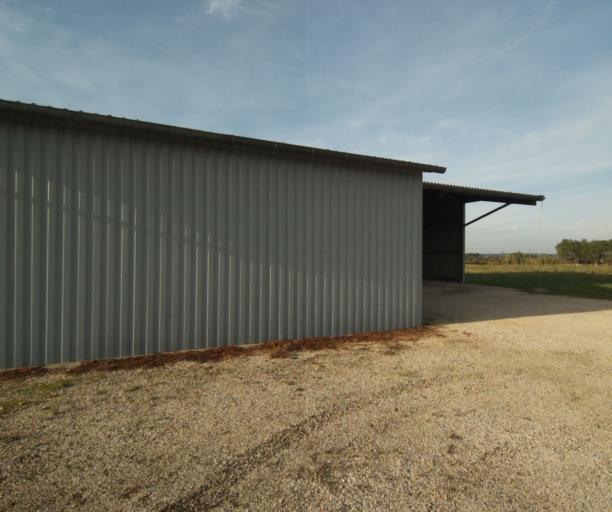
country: FR
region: Midi-Pyrenees
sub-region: Departement du Tarn-et-Garonne
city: Campsas
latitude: 43.8776
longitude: 1.3470
